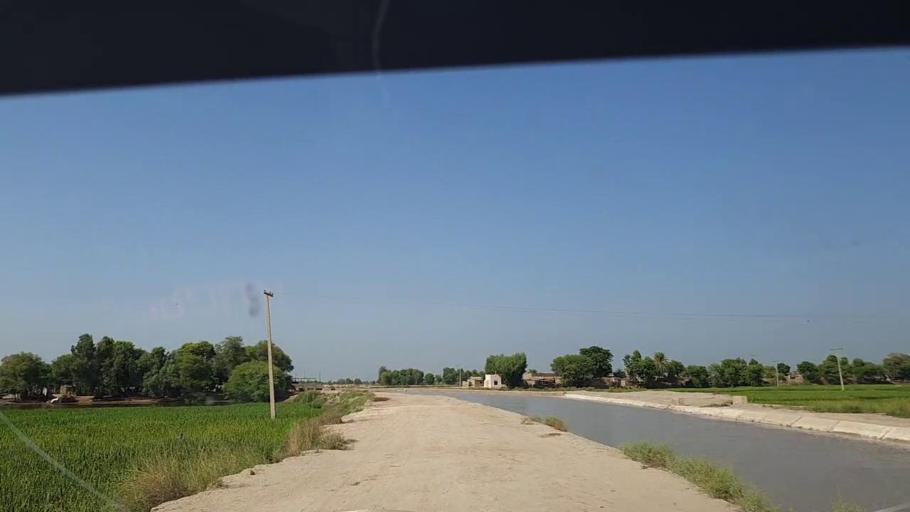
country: PK
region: Sindh
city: Ghauspur
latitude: 28.1734
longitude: 69.0990
